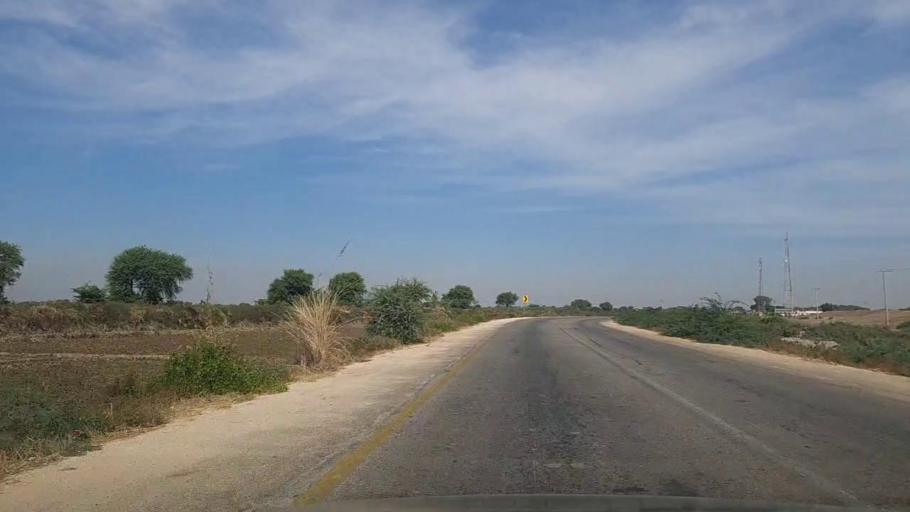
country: PK
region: Sindh
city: Daro Mehar
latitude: 24.9638
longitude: 68.1185
